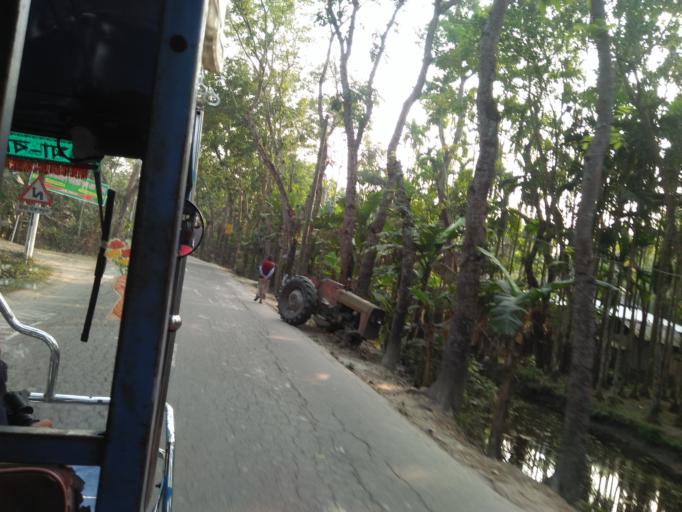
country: BD
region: Barisal
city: Bhola
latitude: 22.7065
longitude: 90.6400
